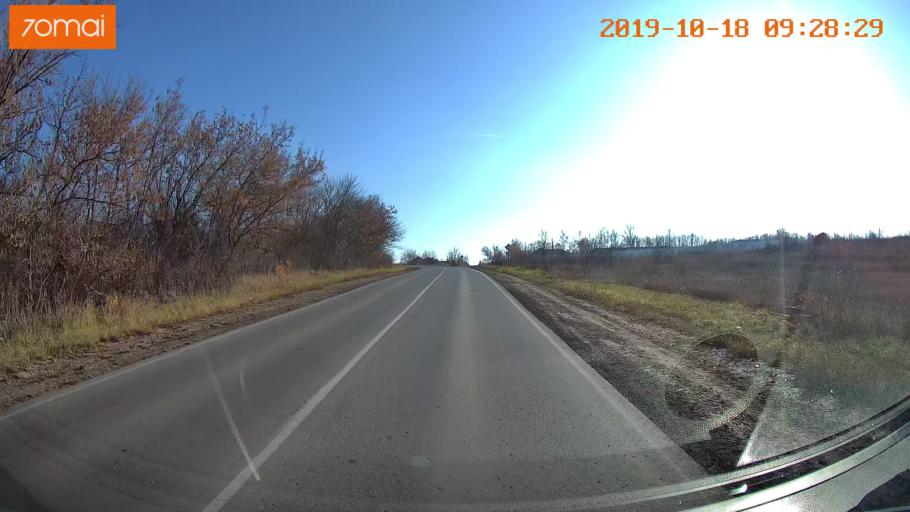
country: RU
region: Tula
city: Yefremov
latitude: 53.1338
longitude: 38.1379
